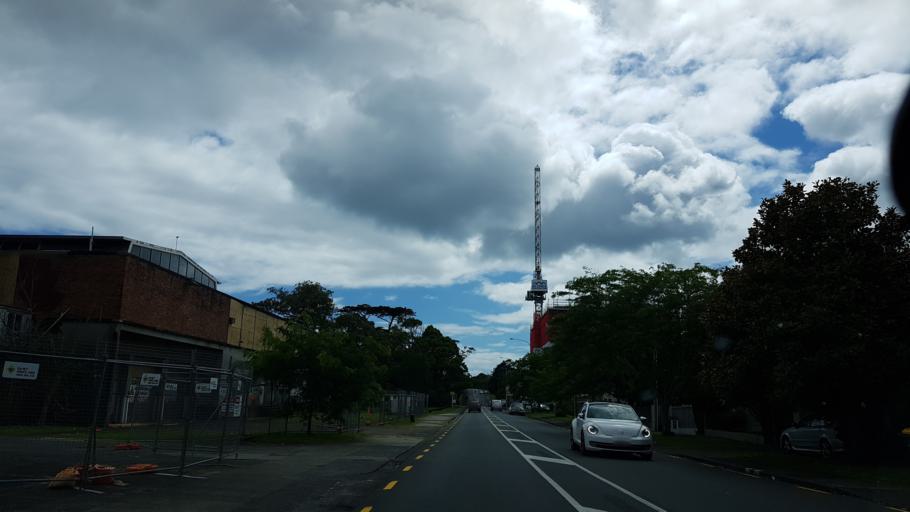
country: NZ
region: Auckland
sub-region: Auckland
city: North Shore
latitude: -36.7879
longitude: 174.7647
